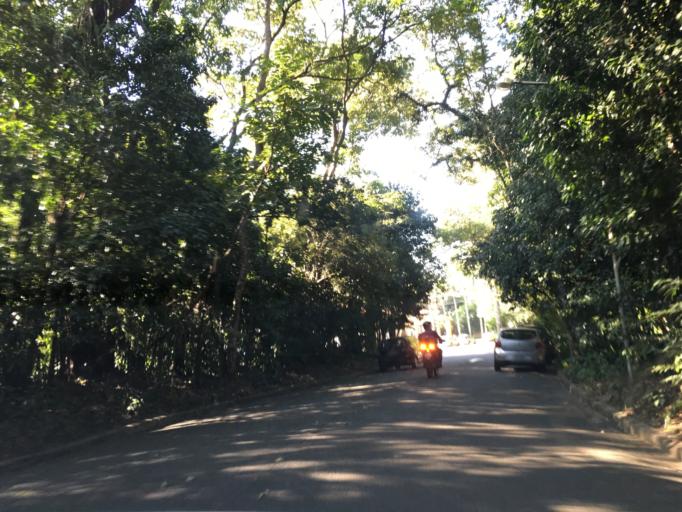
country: BR
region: Sao Paulo
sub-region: Piracicaba
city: Piracicaba
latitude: -22.7108
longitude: -47.6348
